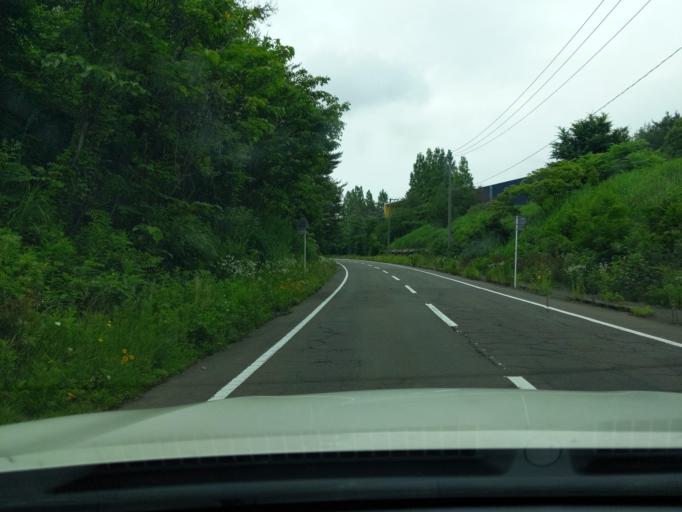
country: JP
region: Niigata
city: Kashiwazaki
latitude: 37.3415
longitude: 138.5946
